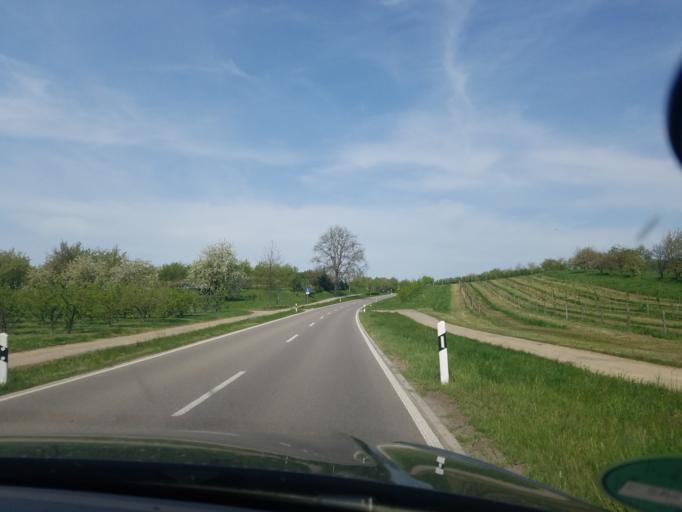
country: DE
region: Baden-Wuerttemberg
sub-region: Freiburg Region
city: Haslach
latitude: 48.5844
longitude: 8.0531
